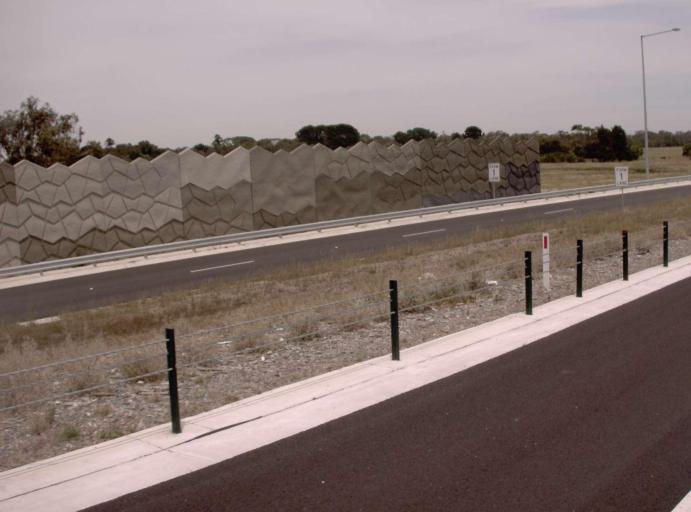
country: AU
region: Victoria
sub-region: Mornington Peninsula
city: Baxter
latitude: -38.1978
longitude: 145.1483
